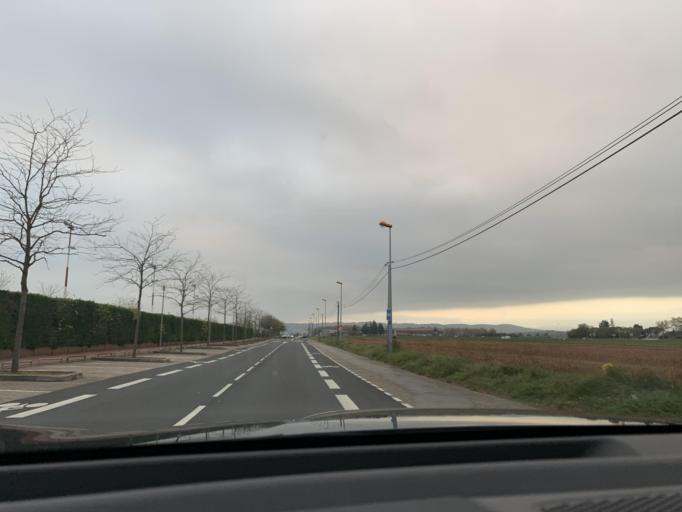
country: FR
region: Rhone-Alpes
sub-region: Departement du Rhone
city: Corbas
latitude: 45.6620
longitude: 4.9111
